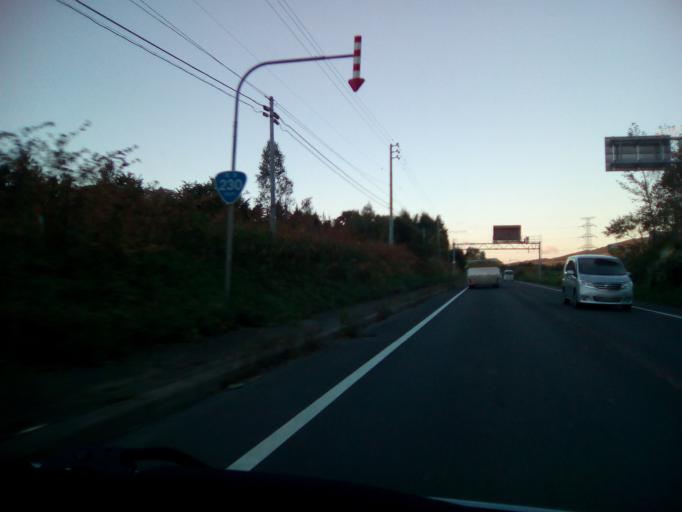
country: JP
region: Hokkaido
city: Niseko Town
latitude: 42.6960
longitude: 140.8413
